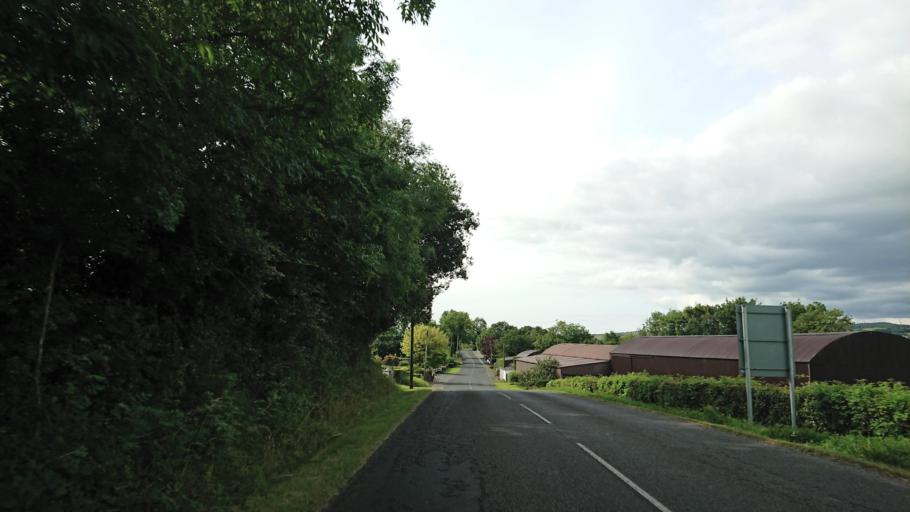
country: GB
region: Northern Ireland
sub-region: Fermanagh District
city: Enniskillen
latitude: 54.2876
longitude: -7.8663
